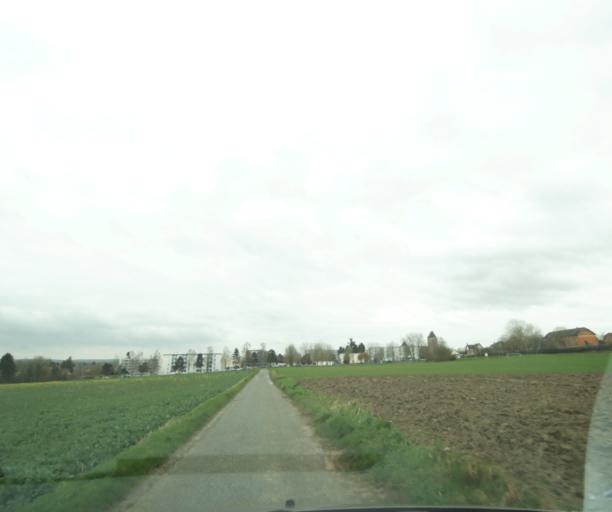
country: FR
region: Picardie
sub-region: Departement de l'Oise
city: Noyon
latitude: 49.5880
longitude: 3.0067
